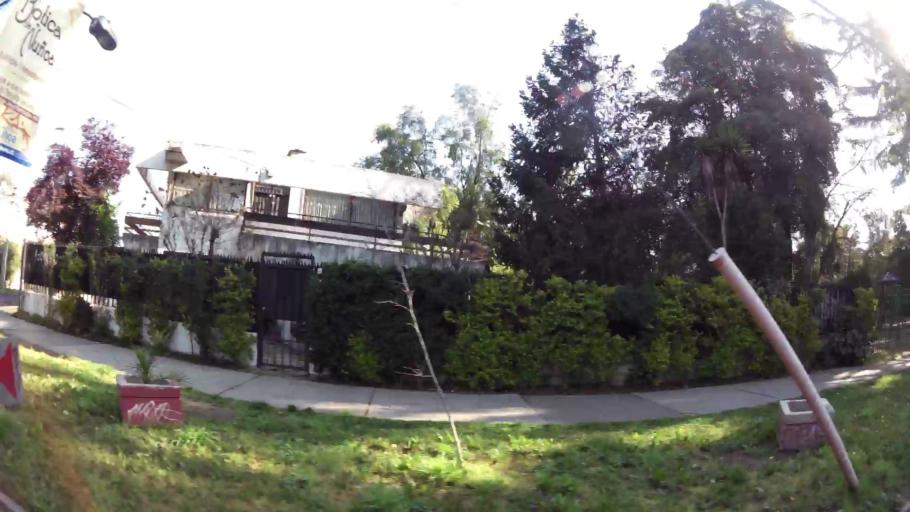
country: CL
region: Santiago Metropolitan
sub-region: Provincia de Santiago
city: Villa Presidente Frei, Nunoa, Santiago, Chile
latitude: -33.4577
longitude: -70.5872
